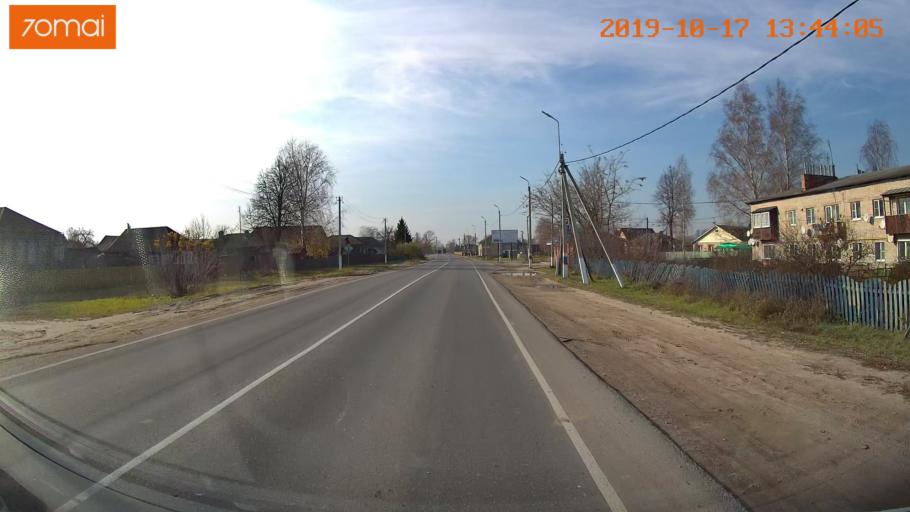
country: RU
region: Rjazan
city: Tuma
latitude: 55.1460
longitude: 40.5340
